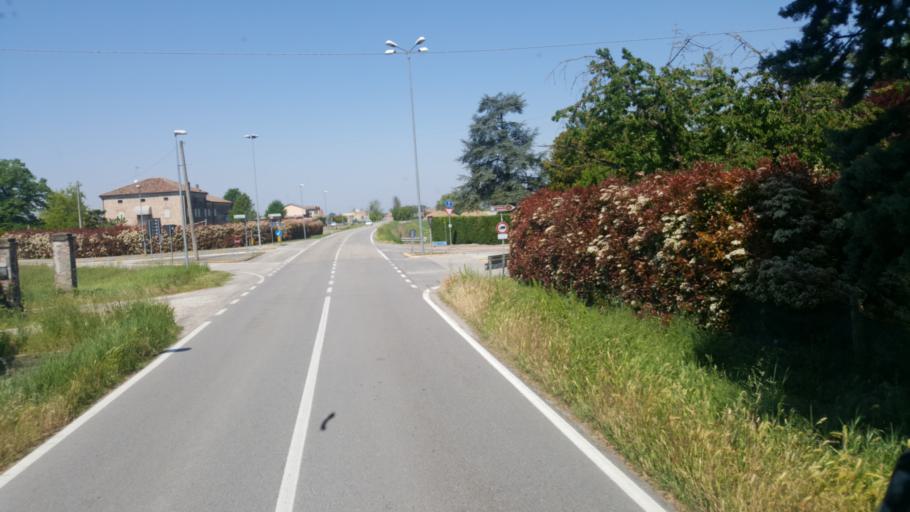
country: IT
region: Lombardy
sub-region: Provincia di Mantova
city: Felonica
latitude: 44.9748
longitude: 11.3446
